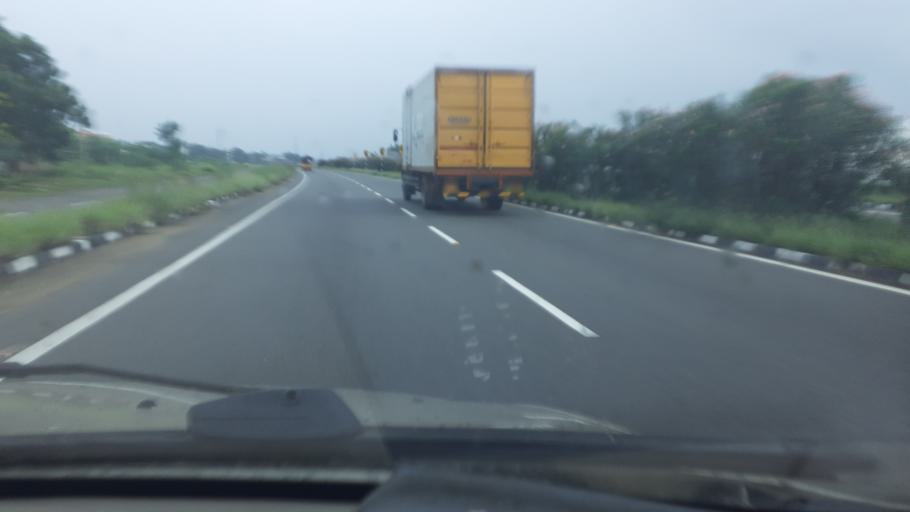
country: IN
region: Tamil Nadu
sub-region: Virudhunagar
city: Virudunagar
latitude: 9.6225
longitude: 77.9580
